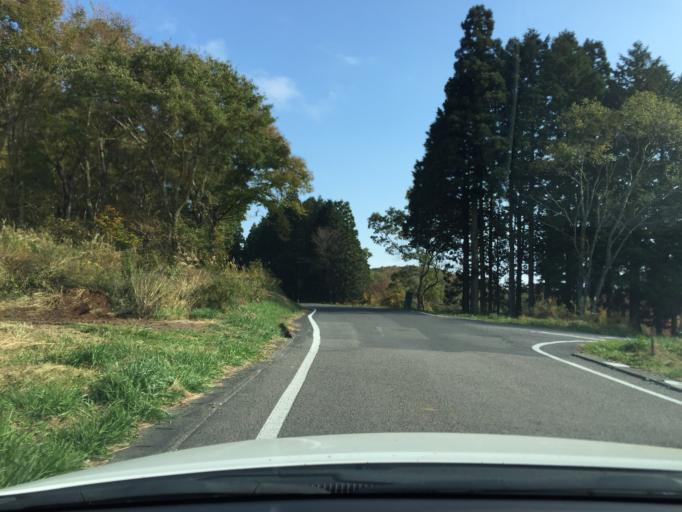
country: JP
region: Fukushima
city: Ishikawa
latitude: 36.9537
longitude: 140.5740
